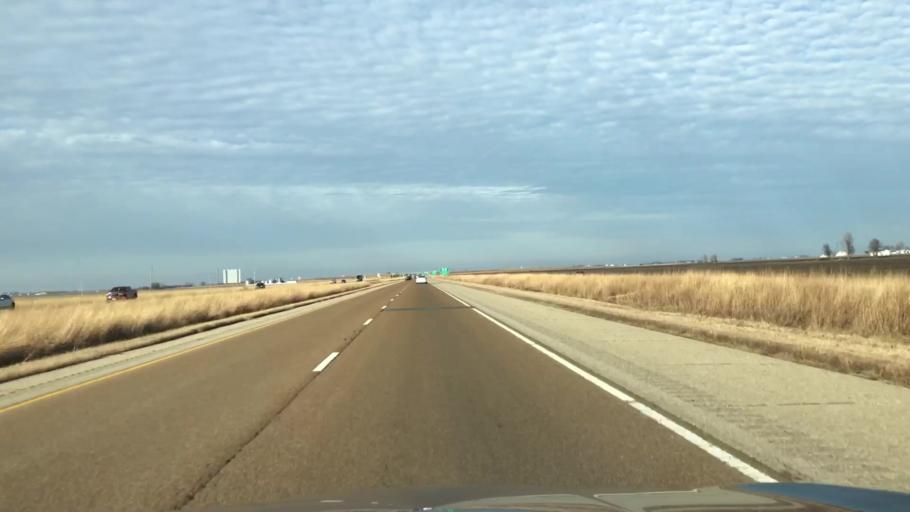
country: US
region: Illinois
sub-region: Montgomery County
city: Raymond
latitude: 39.3043
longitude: -89.6421
